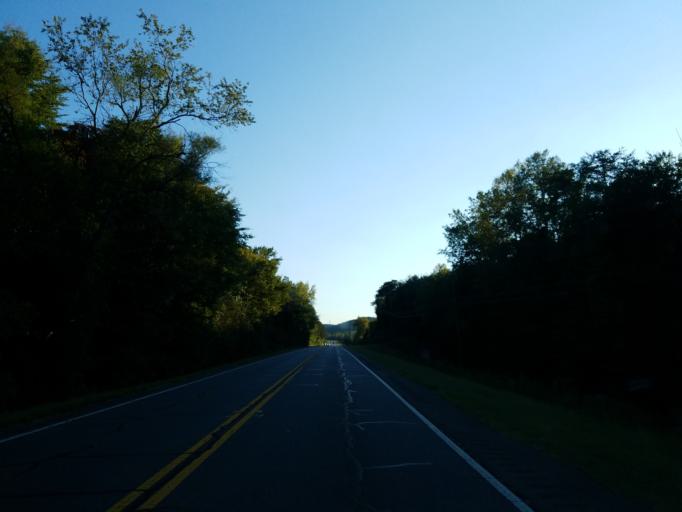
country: US
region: Georgia
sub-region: Bartow County
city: Rydal
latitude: 34.4108
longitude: -84.7009
